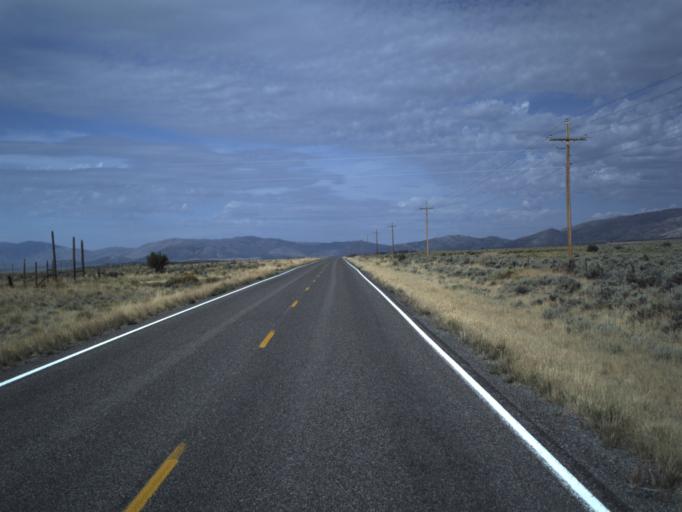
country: US
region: Idaho
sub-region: Cassia County
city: Burley
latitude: 41.8166
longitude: -113.3625
